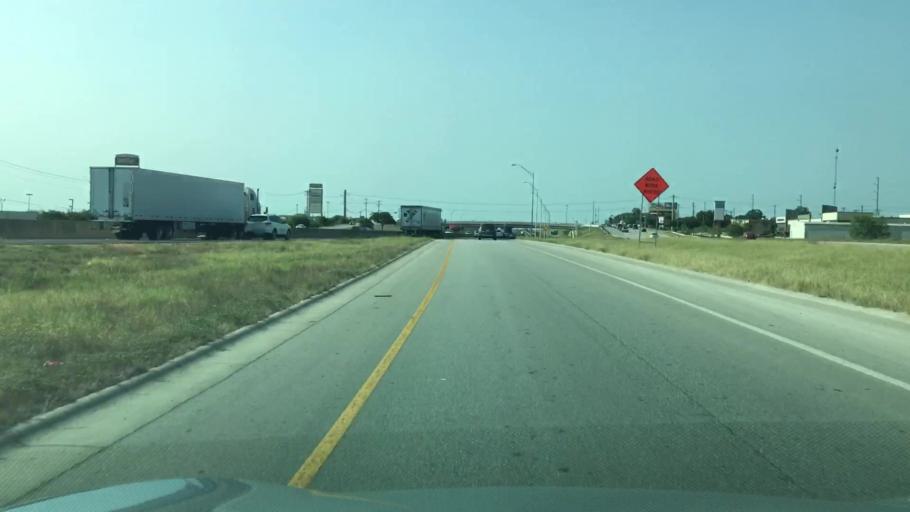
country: US
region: Texas
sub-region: Hays County
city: Kyle
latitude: 29.9923
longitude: -97.8720
